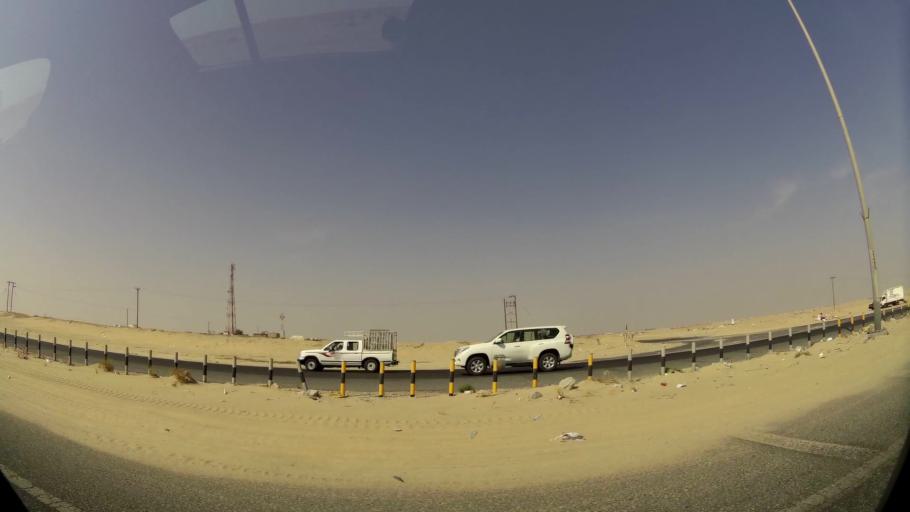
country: KW
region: Al Ahmadi
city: Al Ahmadi
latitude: 28.8440
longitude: 48.0609
